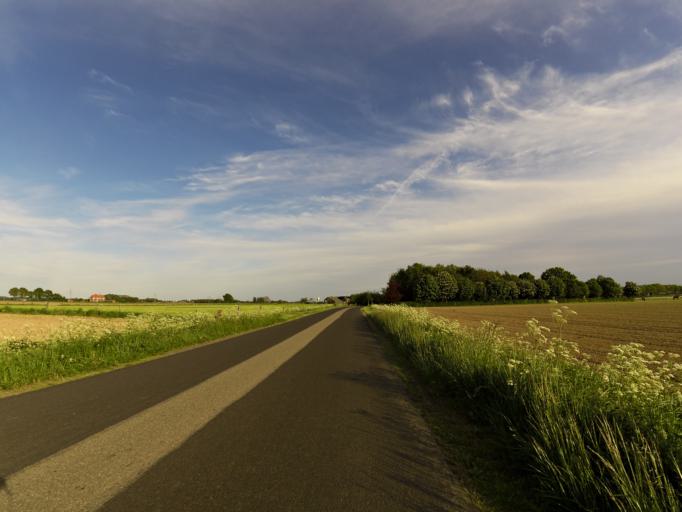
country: NL
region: Gelderland
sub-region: Gemeente Doetinchem
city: Doetinchem
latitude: 51.9340
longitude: 6.2801
